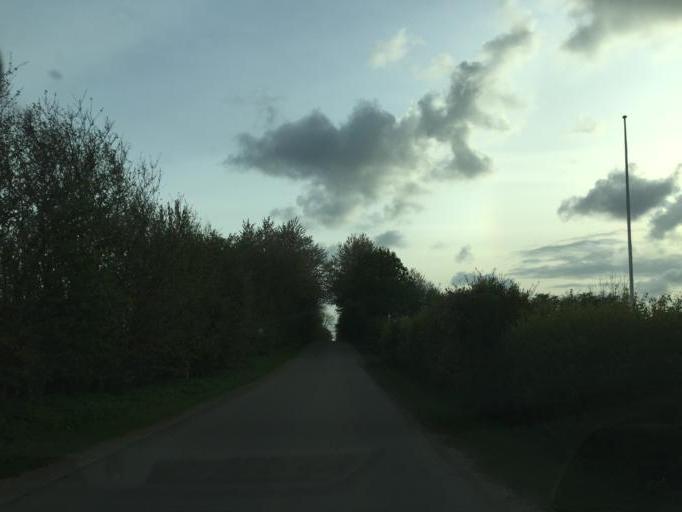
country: DK
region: South Denmark
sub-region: Svendborg Kommune
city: Svendborg
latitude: 55.1536
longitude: 10.5668
